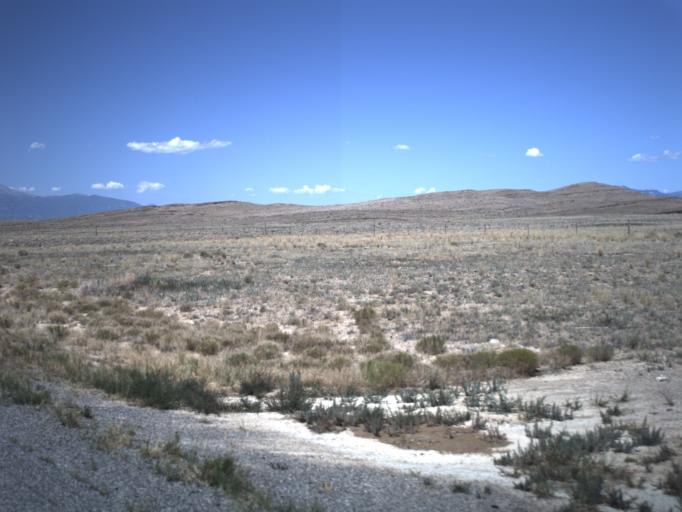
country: US
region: Utah
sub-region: Beaver County
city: Milford
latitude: 39.0455
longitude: -113.7983
